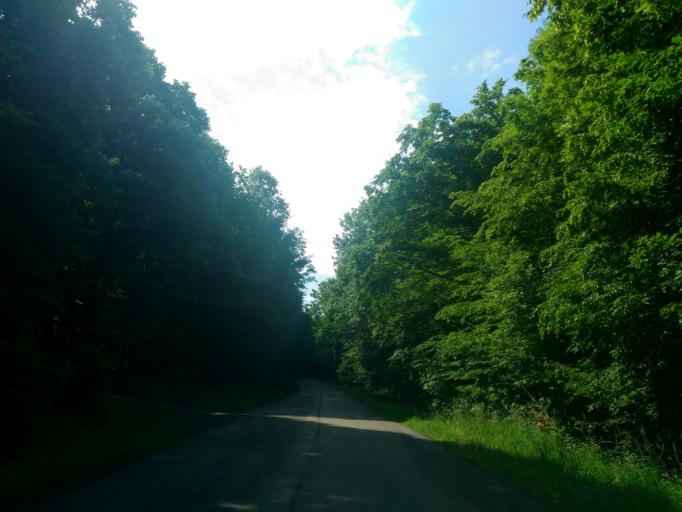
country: HU
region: Baranya
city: Pecs
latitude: 46.1293
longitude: 18.2283
